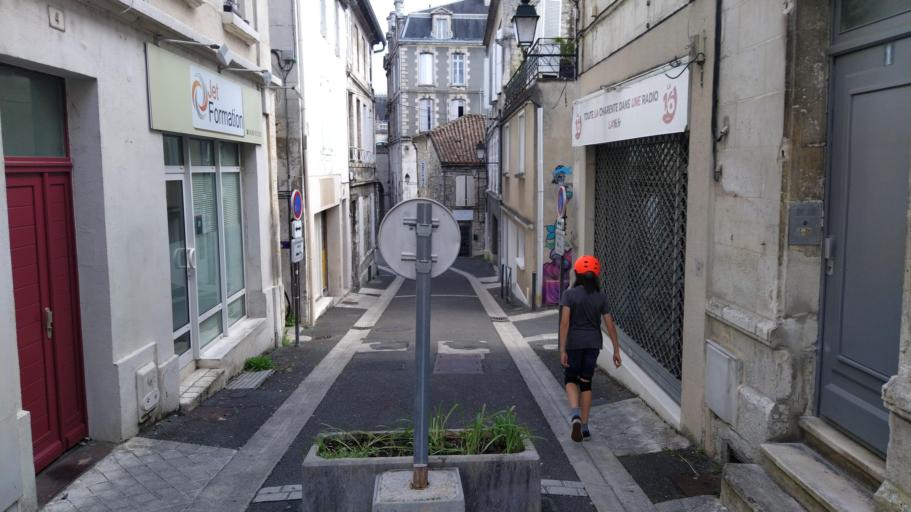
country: FR
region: Poitou-Charentes
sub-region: Departement de la Charente
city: Angouleme
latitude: 45.6482
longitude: 0.1588
